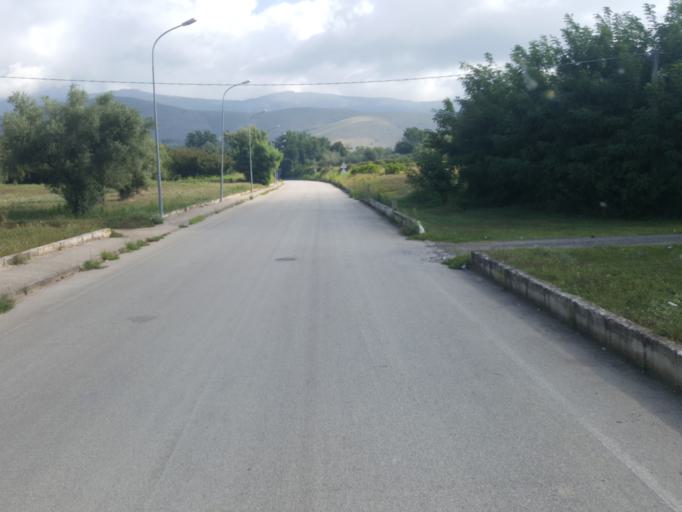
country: IT
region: Campania
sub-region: Provincia di Caserta
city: Pignataro Maggiore
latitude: 41.1820
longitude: 14.1576
